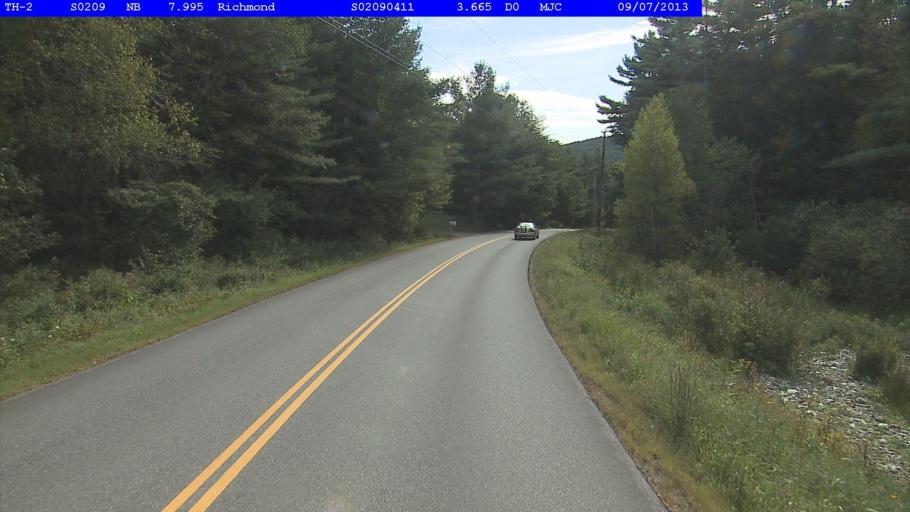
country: US
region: Vermont
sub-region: Chittenden County
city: Williston
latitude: 44.3993
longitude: -73.0176
